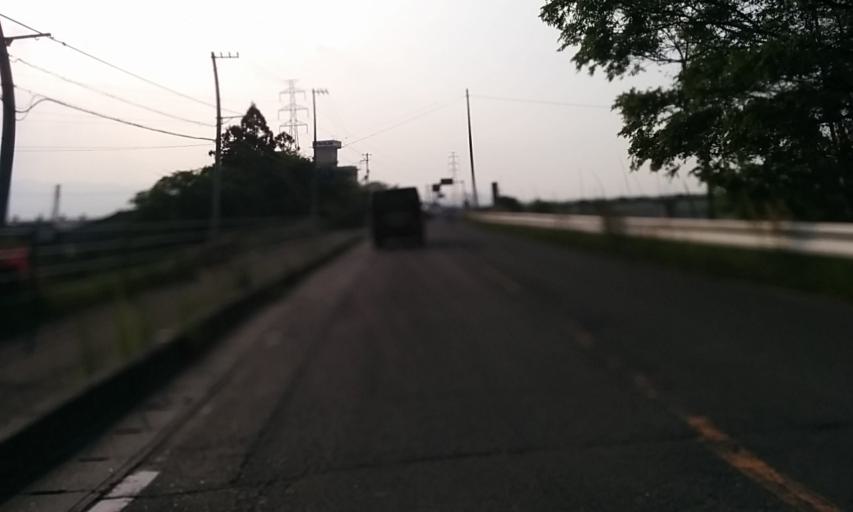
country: JP
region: Ehime
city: Saijo
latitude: 33.9010
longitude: 133.1862
